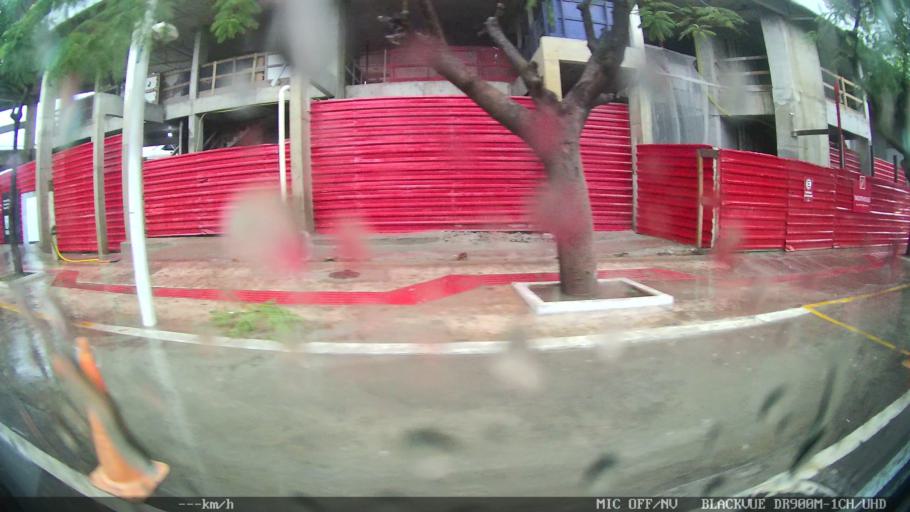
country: BR
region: Santa Catarina
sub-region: Balneario Camboriu
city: Balneario Camboriu
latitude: -27.0072
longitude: -48.6069
